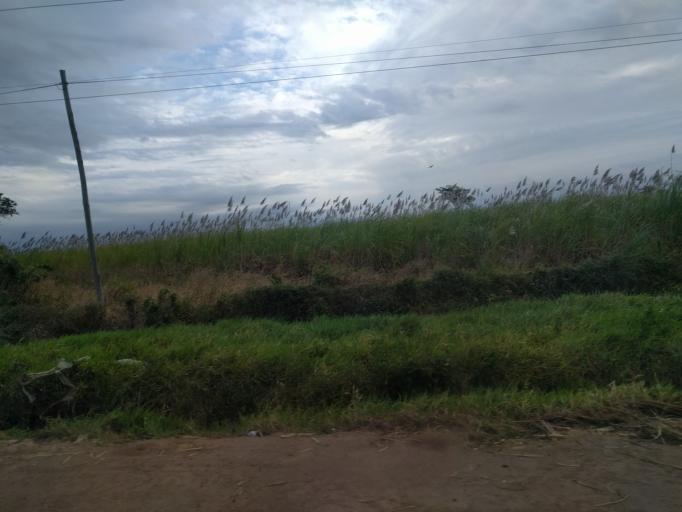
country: BO
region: Santa Cruz
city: Warnes
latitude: -17.4544
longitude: -63.1890
